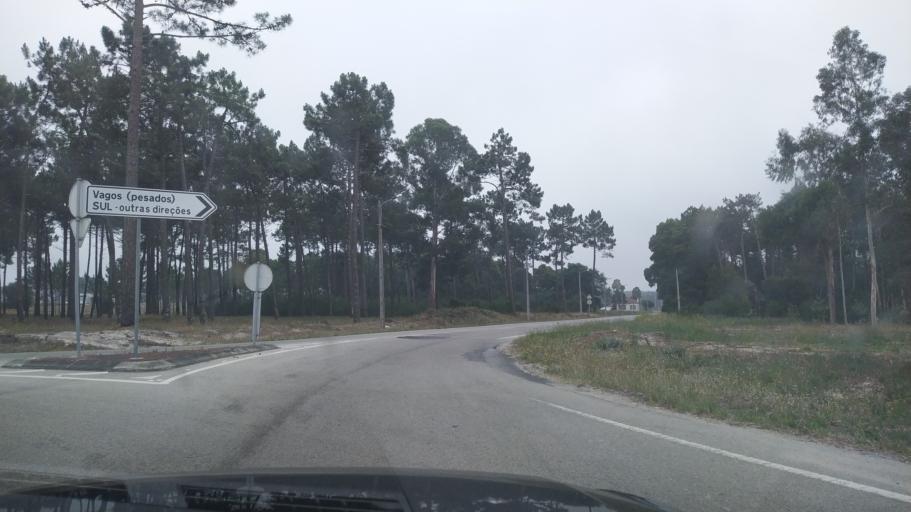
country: PT
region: Aveiro
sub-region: Ilhavo
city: Gafanha da Encarnacao
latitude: 40.6064
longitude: -8.7219
